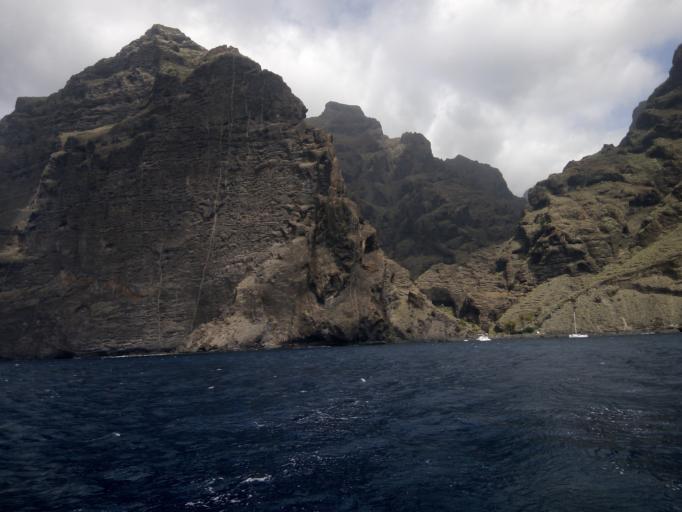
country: ES
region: Canary Islands
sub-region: Provincia de Santa Cruz de Tenerife
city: Santiago del Teide
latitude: 28.2852
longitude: -16.8668
